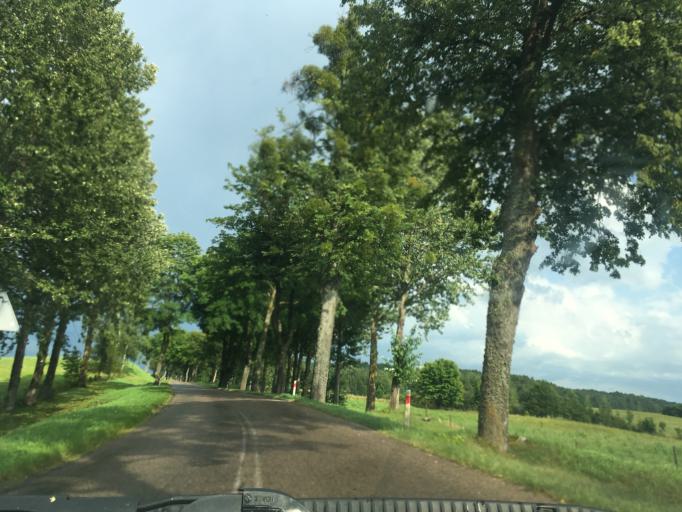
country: PL
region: Warmian-Masurian Voivodeship
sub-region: Powiat olecki
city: Swietajno
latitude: 54.0297
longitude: 22.2381
